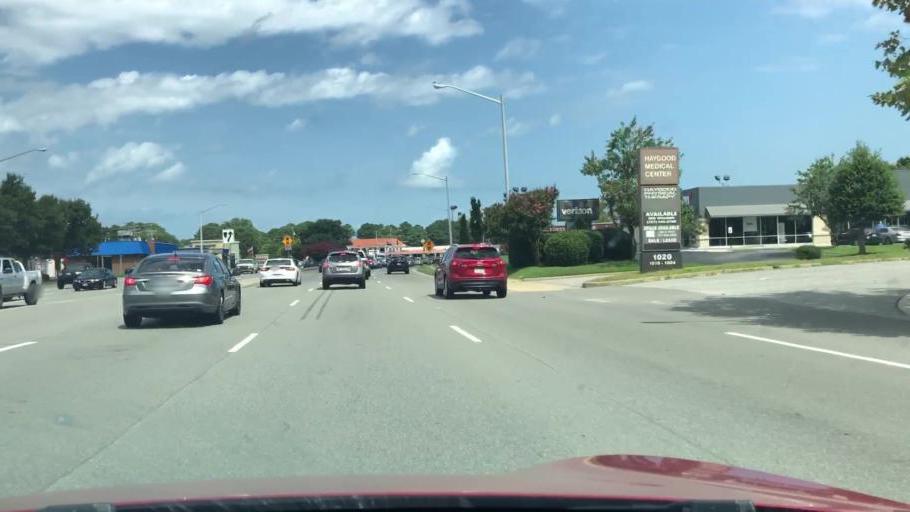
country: US
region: Virginia
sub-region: City of Chesapeake
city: Chesapeake
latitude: 36.8729
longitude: -76.1341
